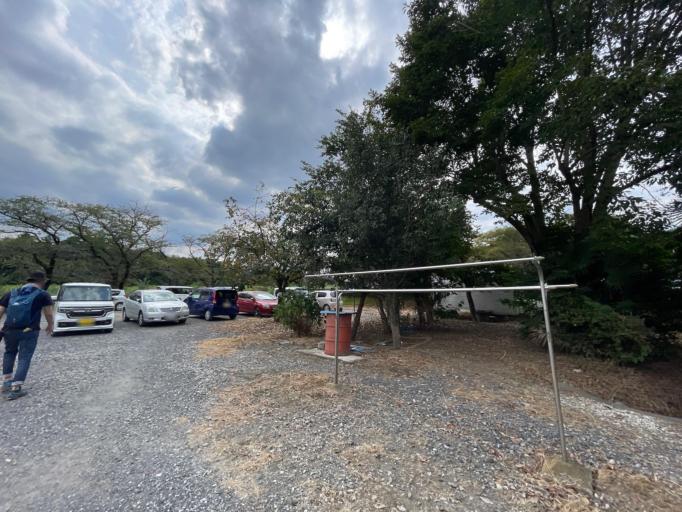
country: JP
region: Saitama
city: Hanno
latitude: 35.8434
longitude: 139.3615
